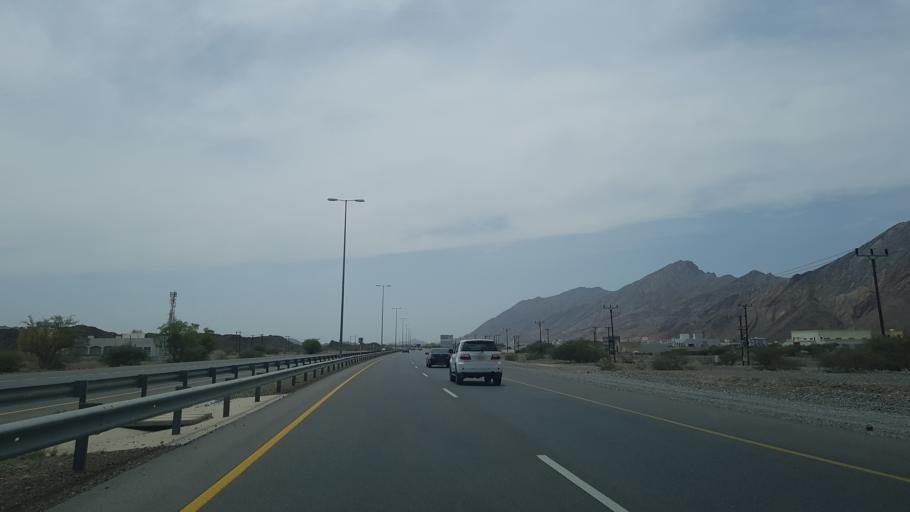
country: OM
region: Muhafazat ad Dakhiliyah
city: Izki
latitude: 23.0326
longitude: 57.7988
